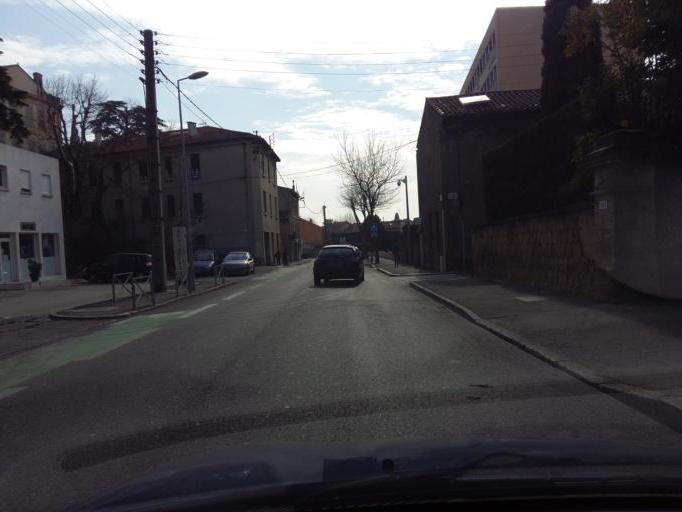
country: FR
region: Provence-Alpes-Cote d'Azur
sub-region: Departement des Bouches-du-Rhone
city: Salon-de-Provence
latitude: 43.6454
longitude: 5.0939
